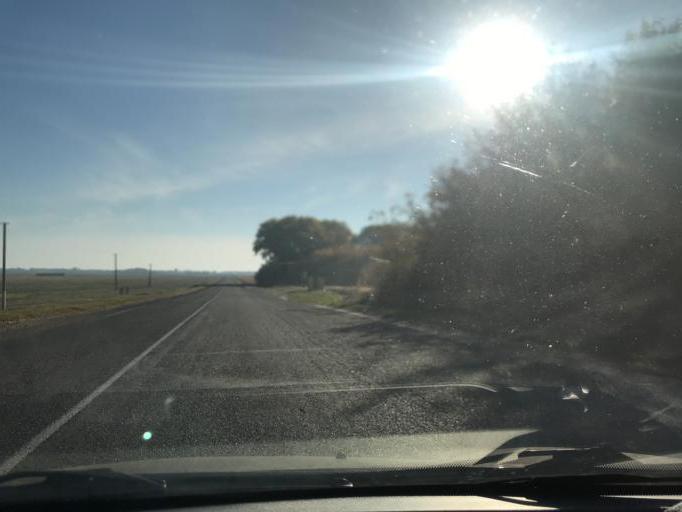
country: BY
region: Gomel
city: Brahin
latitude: 51.7825
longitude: 30.2191
